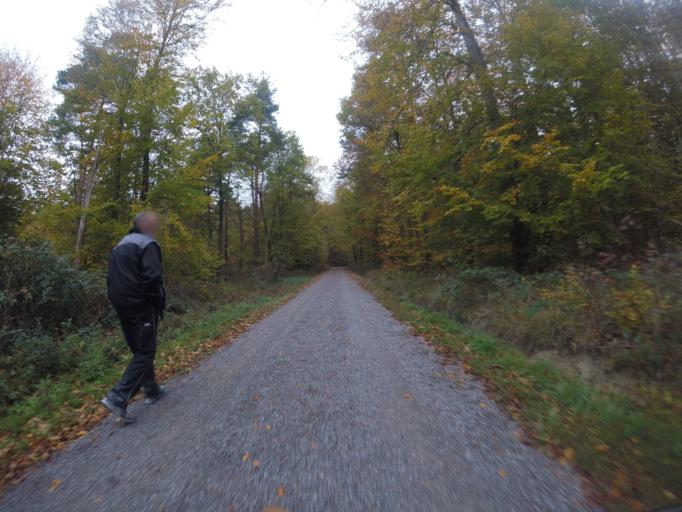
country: DE
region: Baden-Wuerttemberg
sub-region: Regierungsbezirk Stuttgart
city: Kirchberg an der Murr
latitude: 48.9700
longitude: 9.3551
